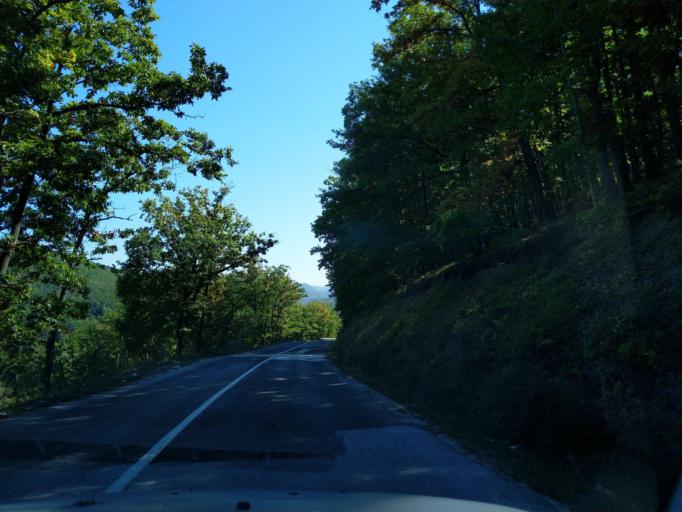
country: RS
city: Sokolovica
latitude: 43.2552
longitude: 20.2541
